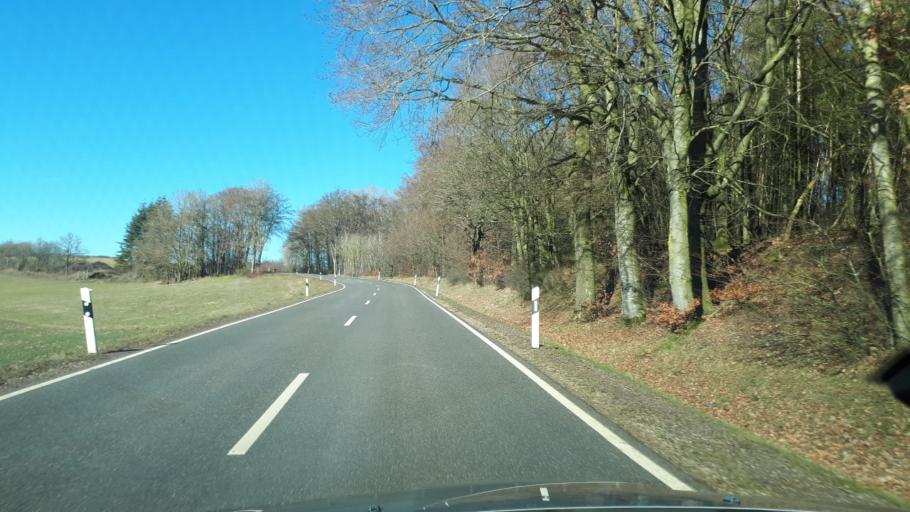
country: DE
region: Rheinland-Pfalz
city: Ellscheid
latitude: 50.1445
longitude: 6.9308
